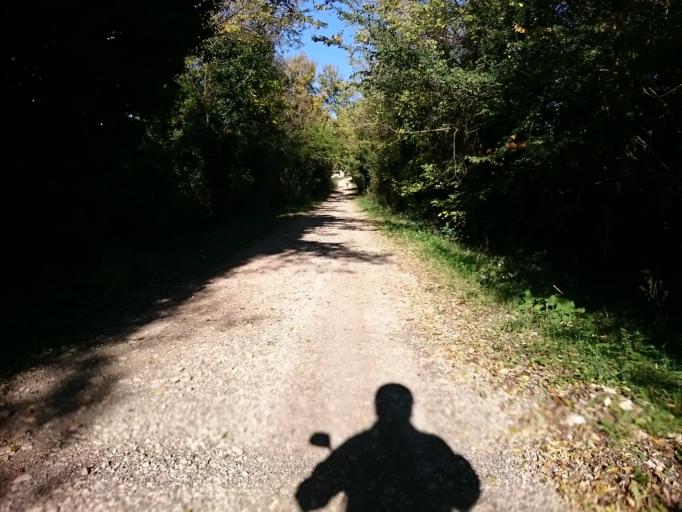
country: HR
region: Istarska
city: Umag
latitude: 45.4676
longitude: 13.5633
